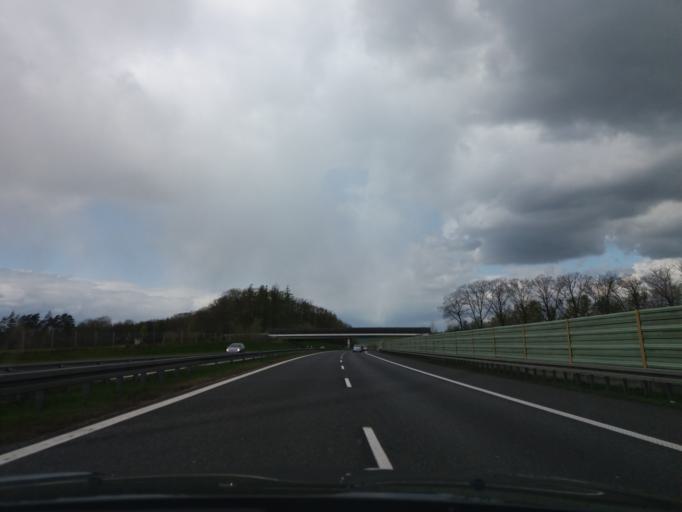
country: PL
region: Silesian Voivodeship
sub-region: Powiat gliwicki
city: Rudziniec
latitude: 50.3816
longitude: 18.4644
